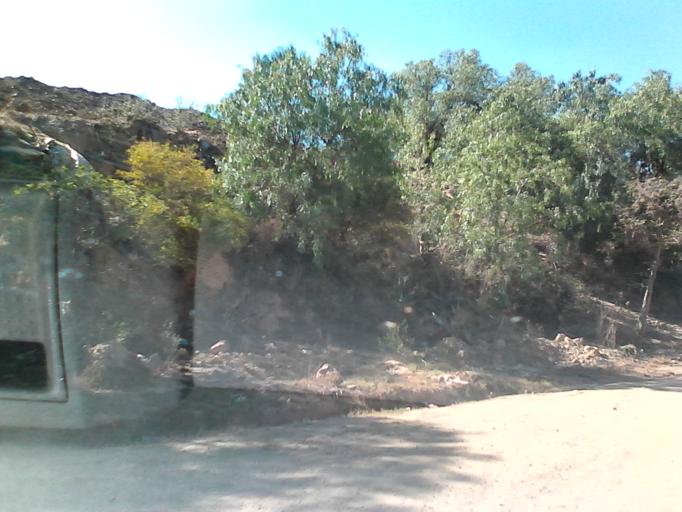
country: CO
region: Boyaca
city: Sachica
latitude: 5.5779
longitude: -73.5421
